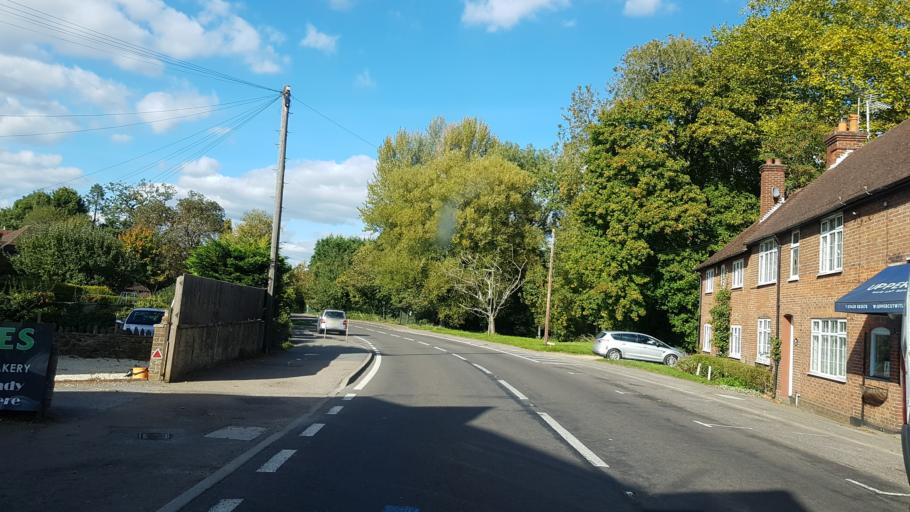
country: GB
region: England
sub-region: Surrey
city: Milford
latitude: 51.1551
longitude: -0.6476
